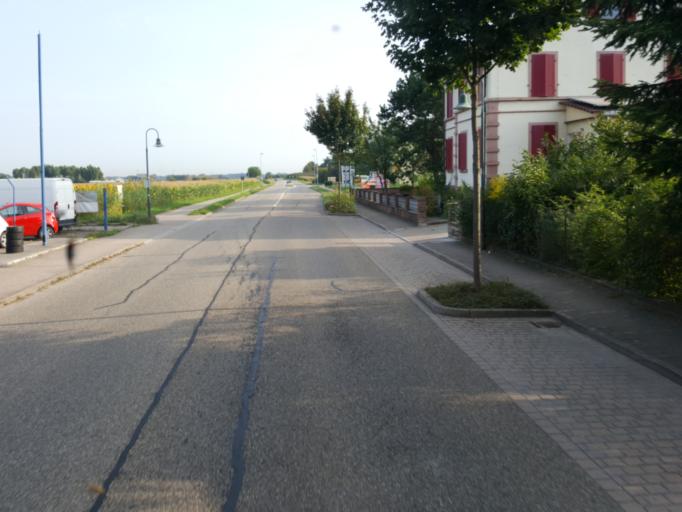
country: DE
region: Baden-Wuerttemberg
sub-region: Freiburg Region
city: Friesenheim
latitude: 48.3759
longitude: 7.8753
